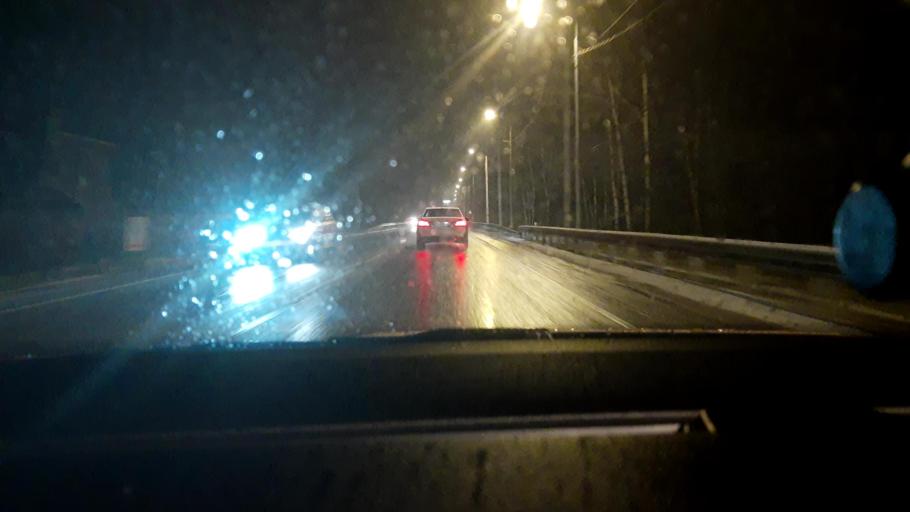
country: RU
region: Moskovskaya
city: Pirogovskiy
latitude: 55.9701
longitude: 37.7010
